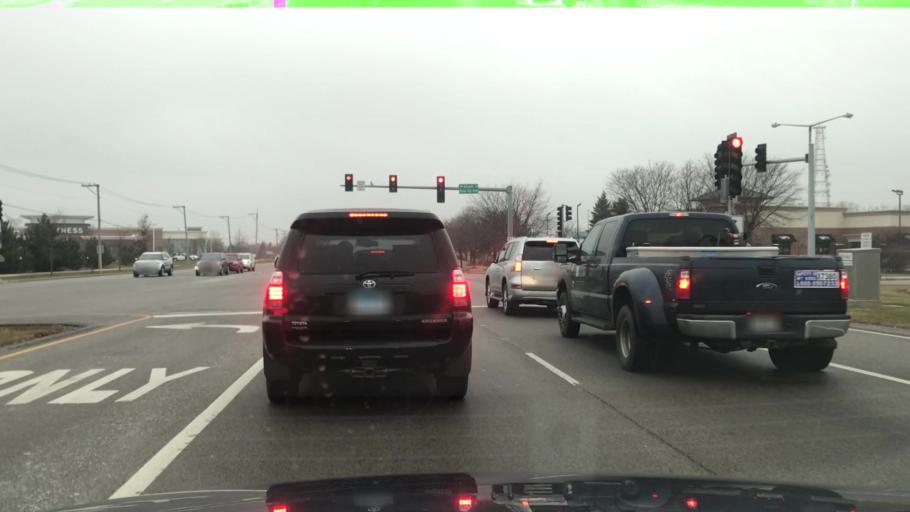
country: US
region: Illinois
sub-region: Lake County
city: Lake Zurich
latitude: 42.1835
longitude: -88.0868
